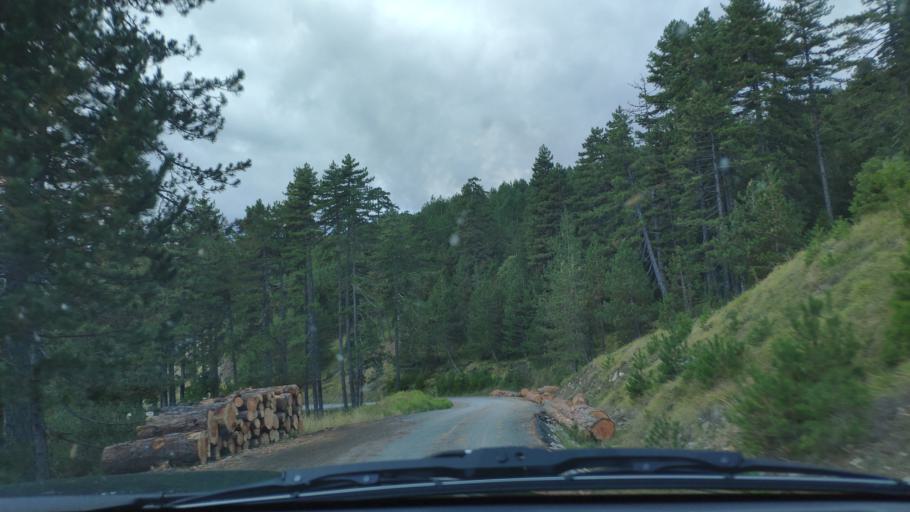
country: AL
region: Korce
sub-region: Rrethi i Kolonjes
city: Erseke
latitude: 40.2894
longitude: 20.8650
